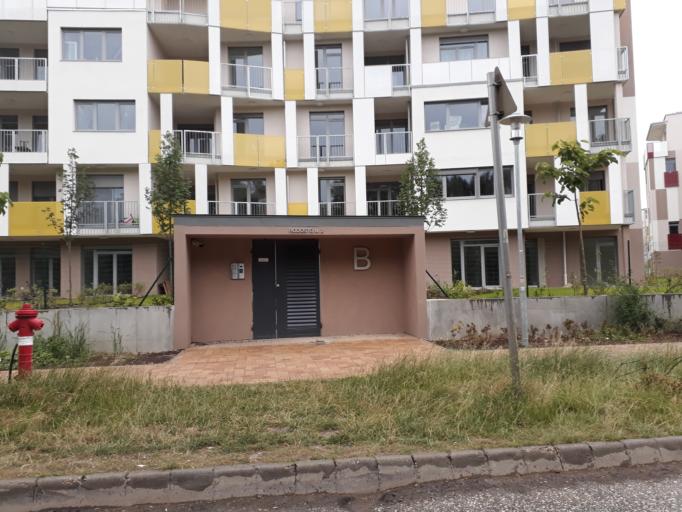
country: HU
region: Budapest
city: Budapest XII. keruelet
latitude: 47.4698
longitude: 19.0075
